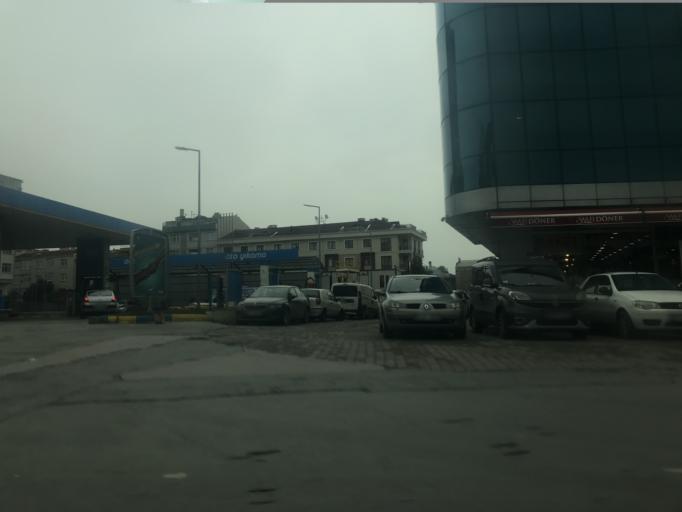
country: TR
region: Istanbul
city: Mahmutbey
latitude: 41.0321
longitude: 28.8340
